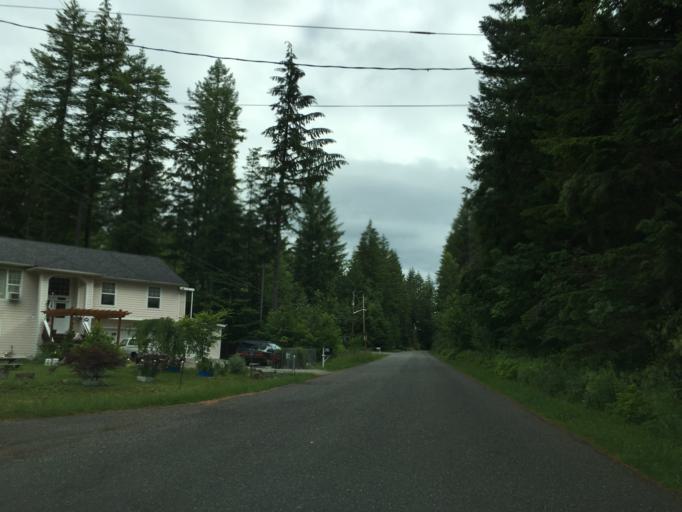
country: US
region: Washington
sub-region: Whatcom County
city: Peaceful Valley
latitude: 48.9402
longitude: -122.1439
